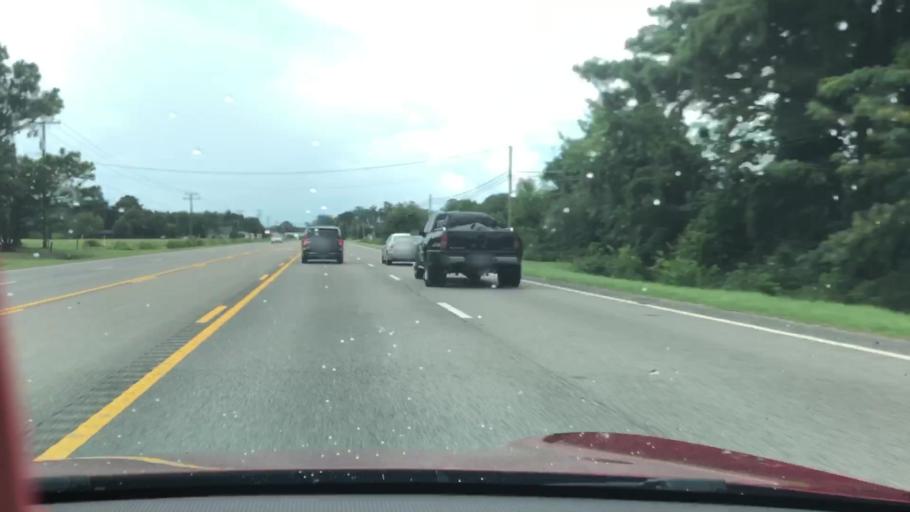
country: US
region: North Carolina
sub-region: Dare County
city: Southern Shores
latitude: 36.1330
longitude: -75.8395
